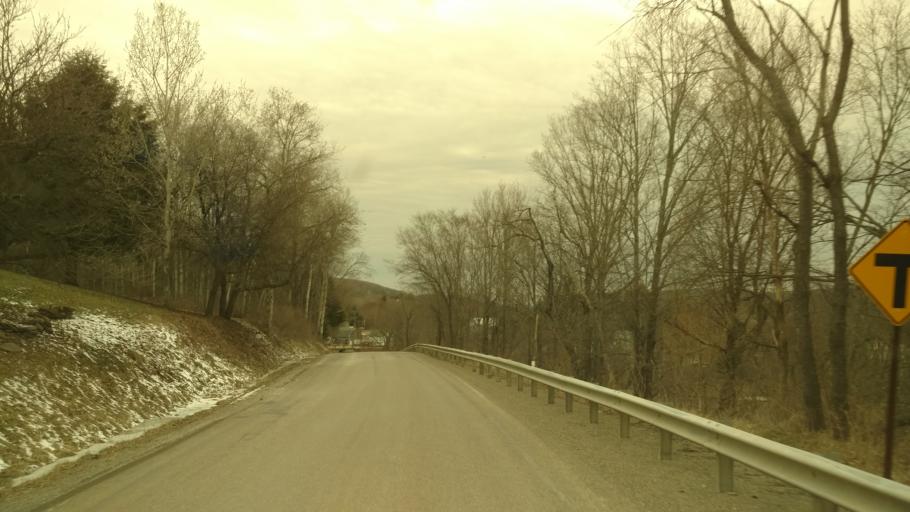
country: US
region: New York
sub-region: Allegany County
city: Wellsville
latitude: 41.9746
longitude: -77.8548
